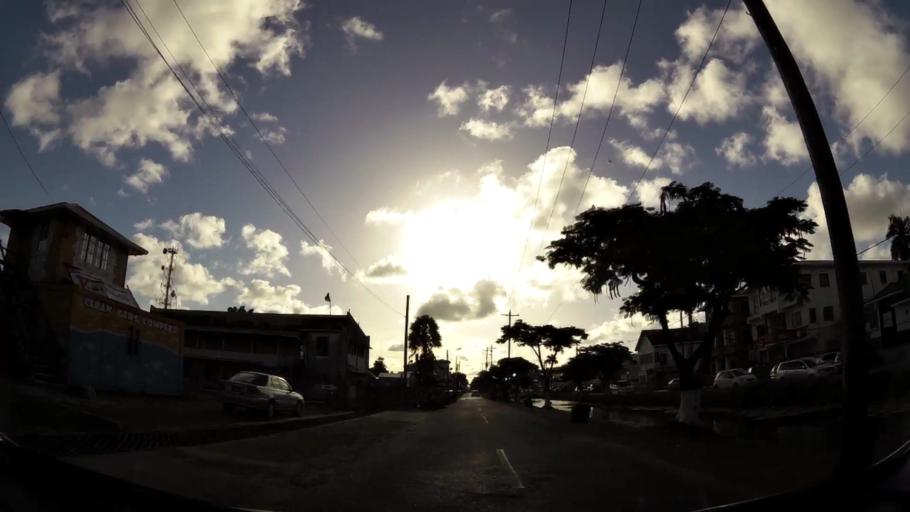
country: GY
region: Demerara-Mahaica
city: Georgetown
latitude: 6.8060
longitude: -58.1518
